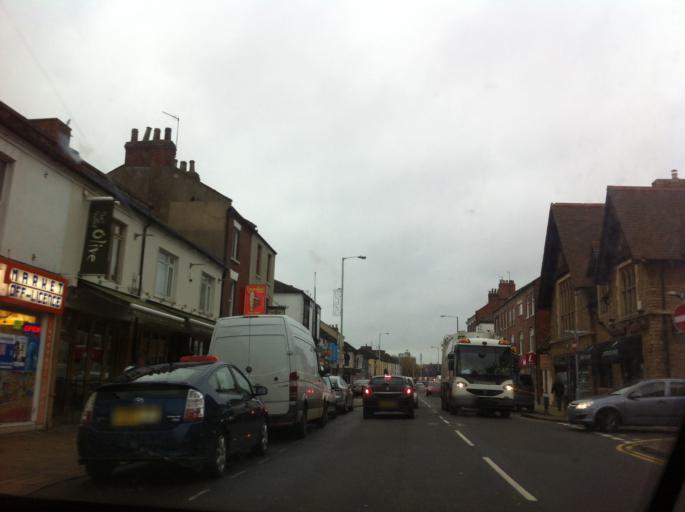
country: GB
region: England
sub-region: Northamptonshire
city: Earls Barton
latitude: 52.2656
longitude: -0.7563
